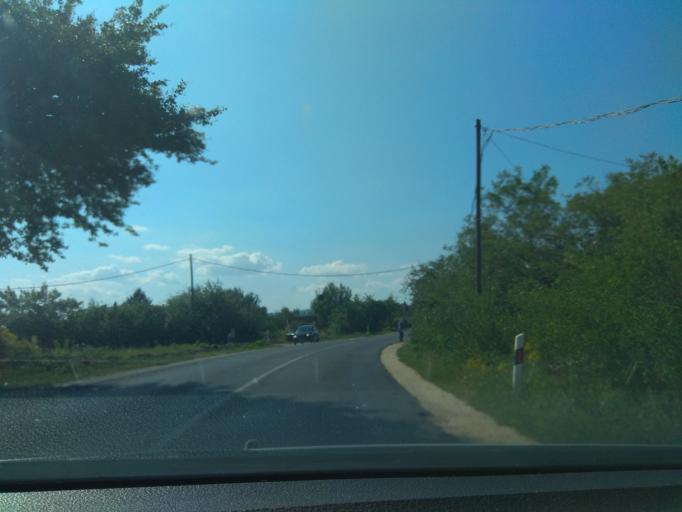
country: HU
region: Borsod-Abauj-Zemplen
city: Malyi
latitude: 48.0376
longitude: 20.7800
